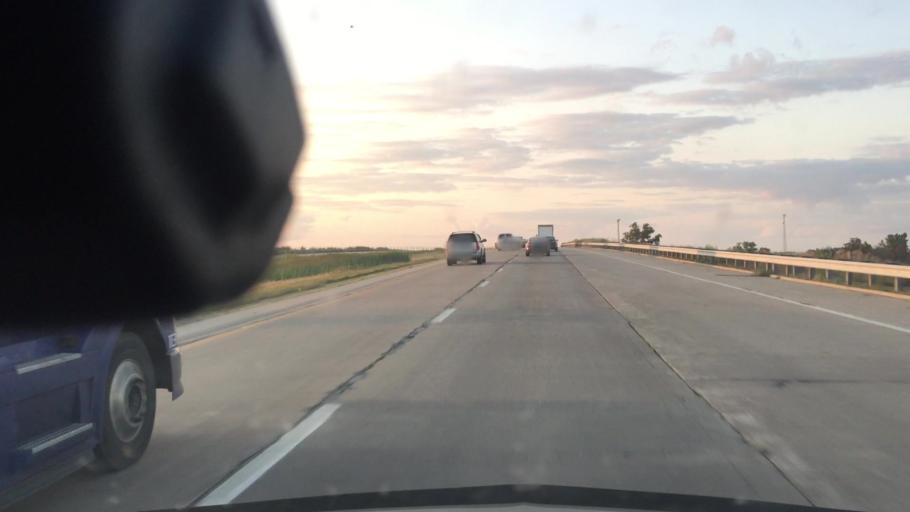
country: US
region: Illinois
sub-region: Livingston County
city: Dwight
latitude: 41.0985
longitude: -88.4497
